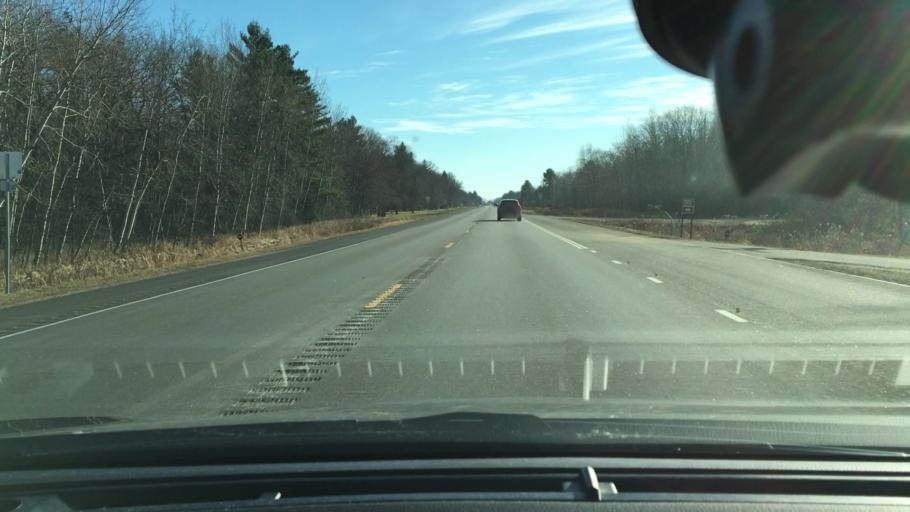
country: US
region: Minnesota
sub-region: Mille Lacs County
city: Vineland
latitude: 46.3106
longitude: -93.8341
